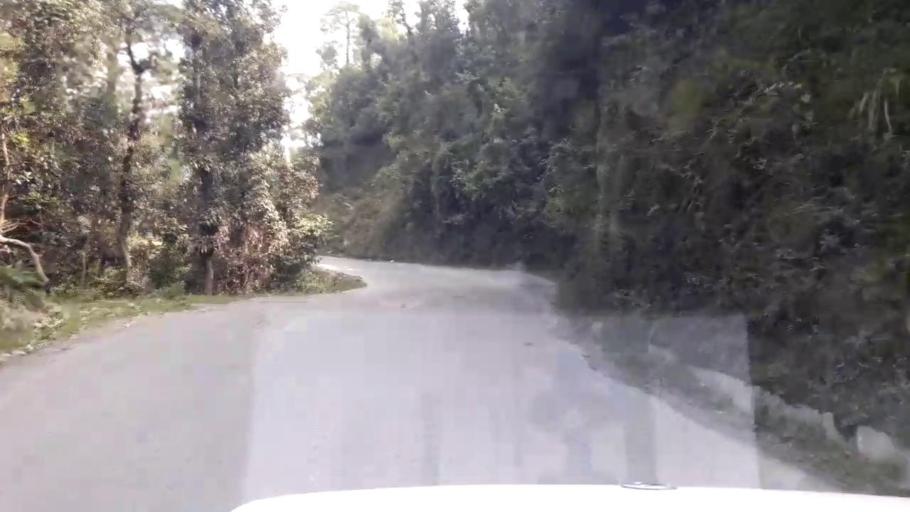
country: IN
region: Himachal Pradesh
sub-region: Shimla
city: Shimla
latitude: 31.0486
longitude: 77.1497
